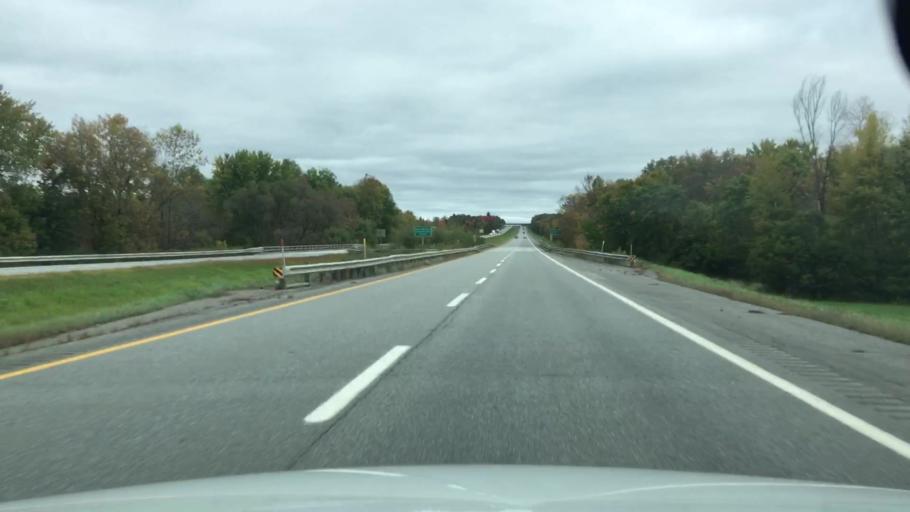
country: US
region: Maine
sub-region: Penobscot County
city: Newport
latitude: 44.8262
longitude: -69.2758
